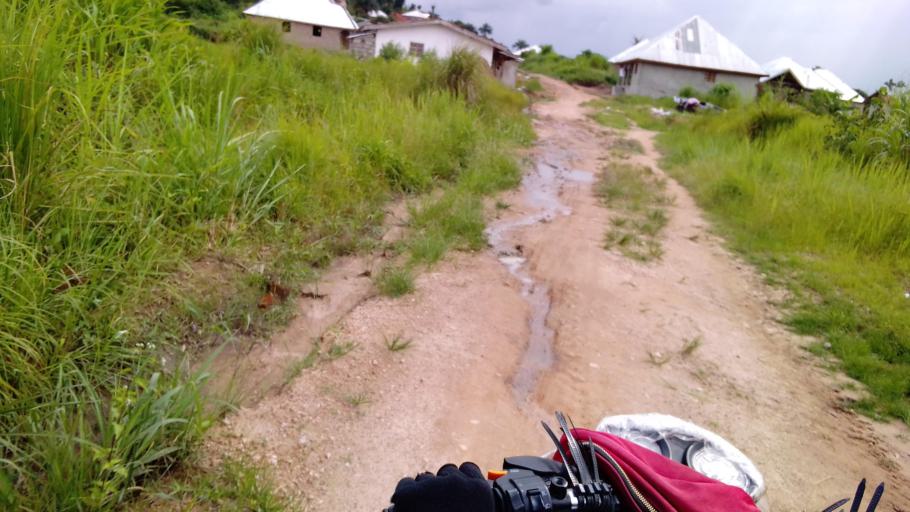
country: SL
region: Eastern Province
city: Koidu
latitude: 8.6688
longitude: -10.9800
